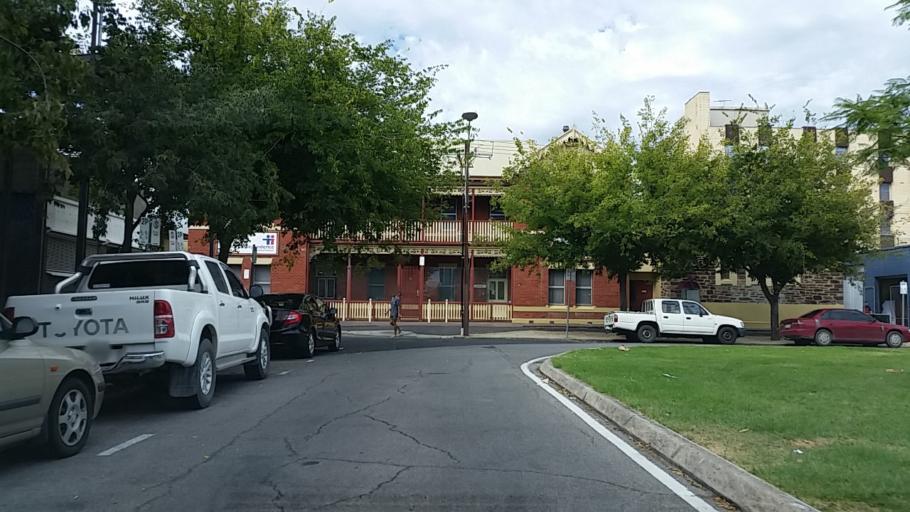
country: AU
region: South Australia
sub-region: Adelaide
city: Adelaide
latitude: -34.9336
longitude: 138.5950
